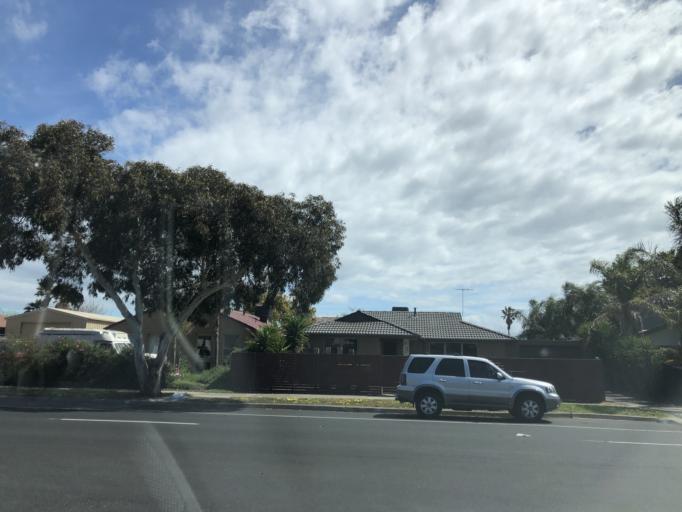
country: AU
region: Victoria
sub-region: Kingston
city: Patterson Lakes
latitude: -38.0732
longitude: 145.1455
